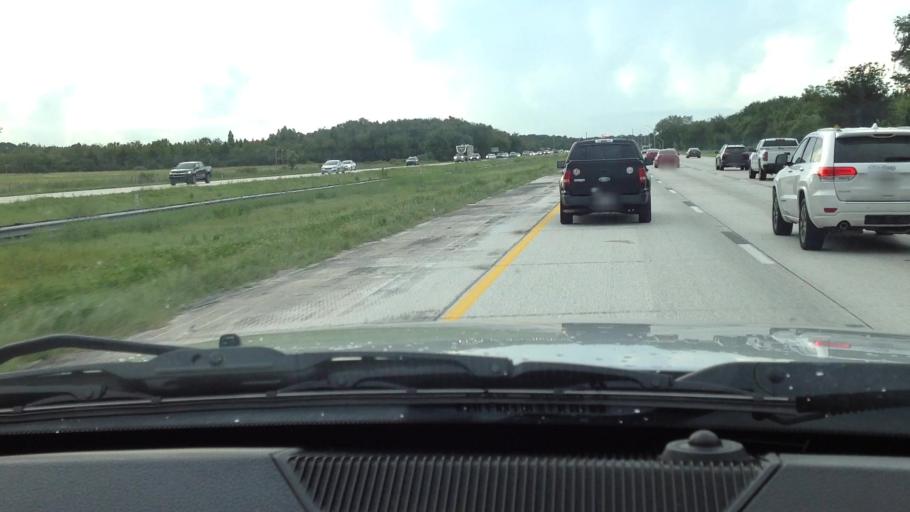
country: US
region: Florida
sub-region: Hillsborough County
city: Mango
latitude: 28.0203
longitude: -82.3347
